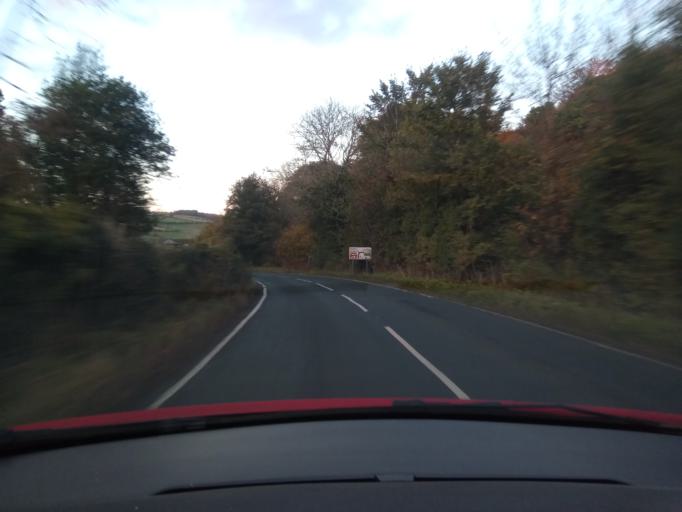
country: GB
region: England
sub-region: Northumberland
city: Bardon Mill
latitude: 54.9658
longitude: -2.2429
